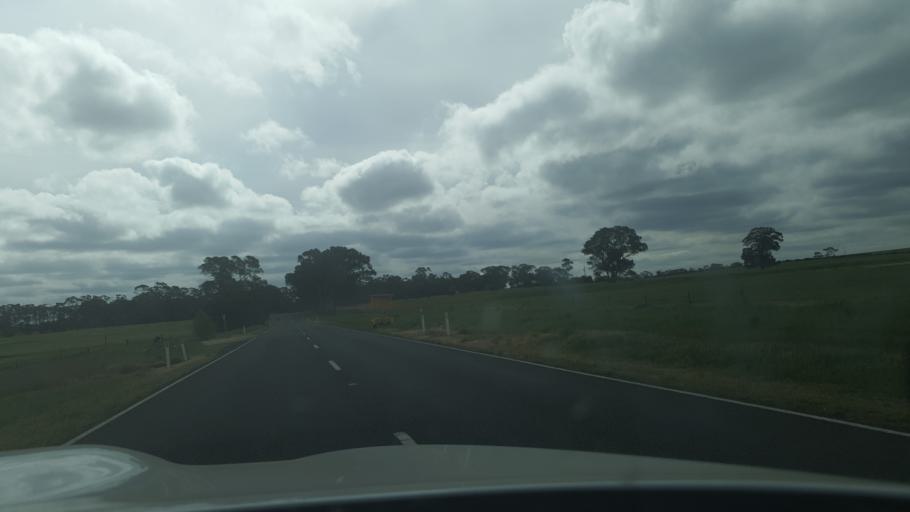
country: AU
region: Victoria
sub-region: Central Goldfields
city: Maryborough
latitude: -37.2056
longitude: 143.7132
